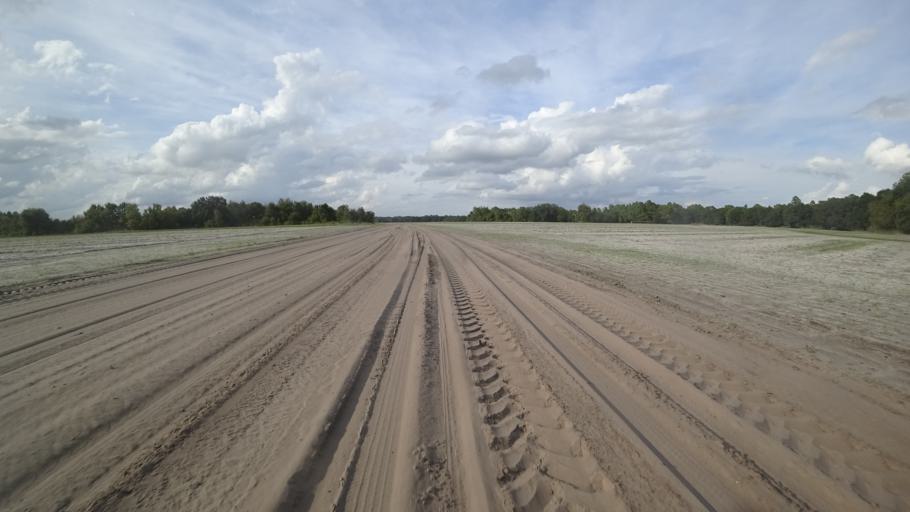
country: US
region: Florida
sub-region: Hillsborough County
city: Wimauma
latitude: 27.6046
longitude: -82.1420
